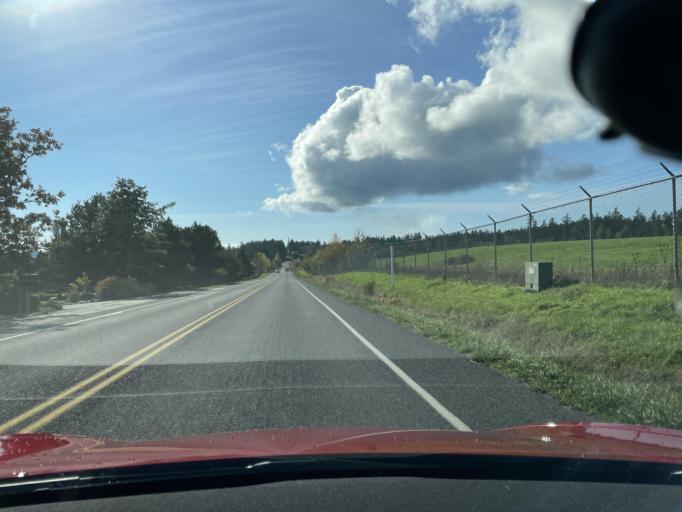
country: US
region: Washington
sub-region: San Juan County
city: Friday Harbor
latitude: 48.5183
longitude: -123.0231
